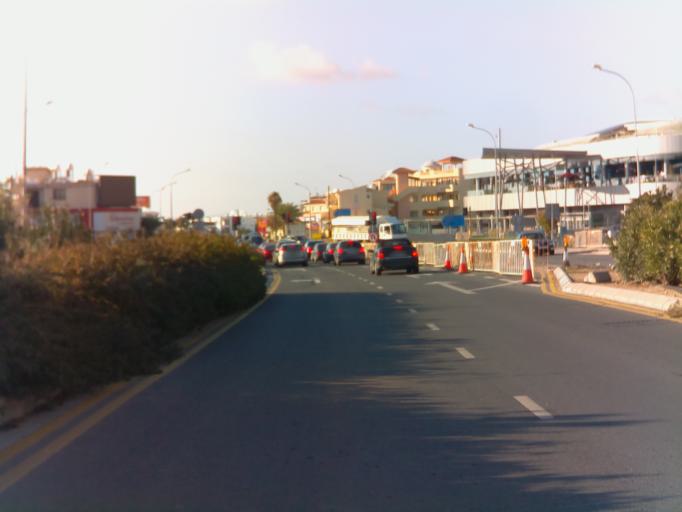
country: CY
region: Pafos
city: Paphos
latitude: 34.7635
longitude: 32.4141
